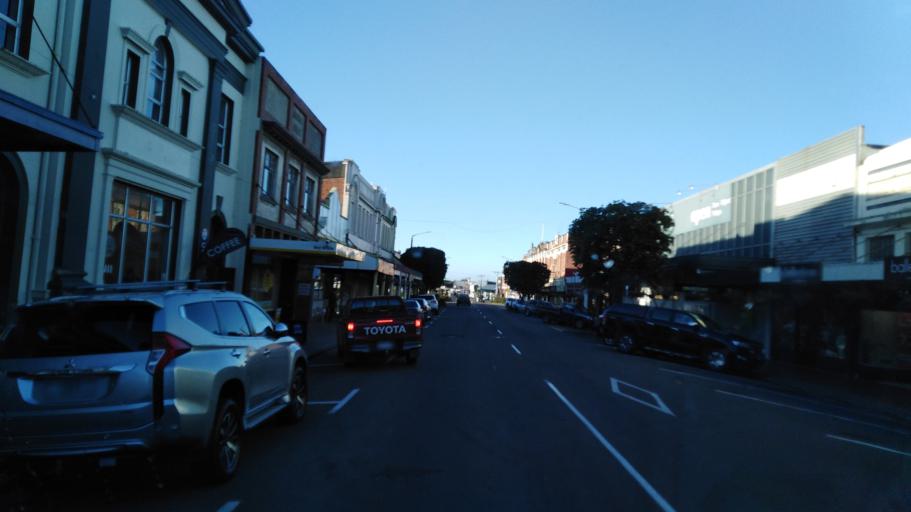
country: NZ
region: Manawatu-Wanganui
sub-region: Rangitikei District
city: Bulls
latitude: -40.0677
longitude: 175.3787
